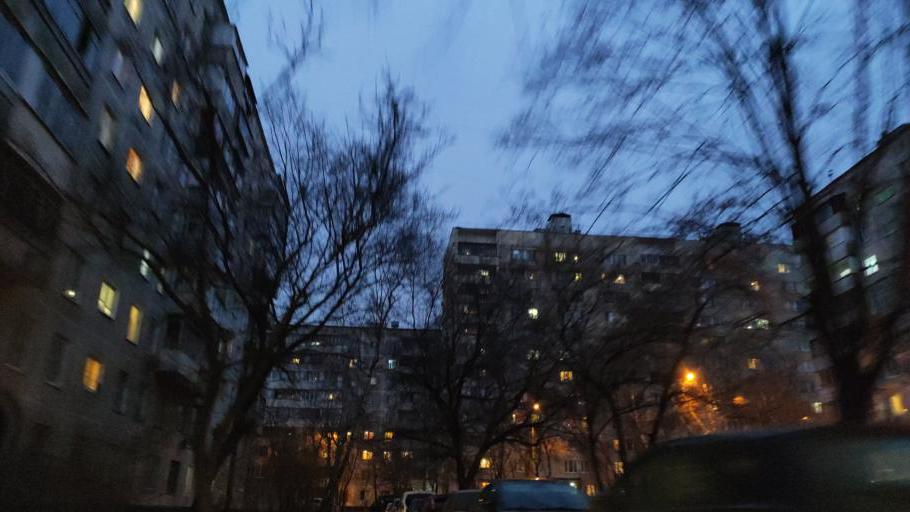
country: RU
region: Moscow
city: Lyublino
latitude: 55.6805
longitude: 37.7686
